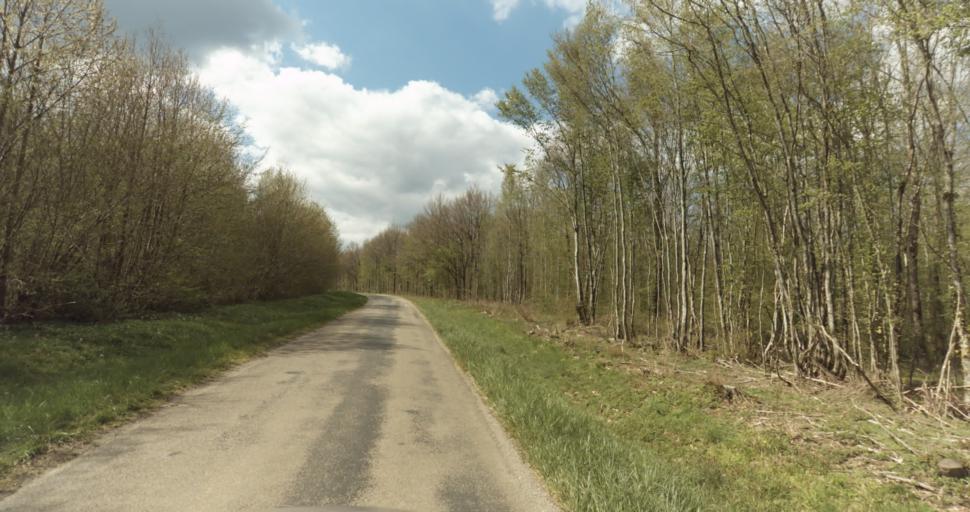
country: FR
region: Bourgogne
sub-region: Departement de la Cote-d'Or
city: Auxonne
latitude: 47.1812
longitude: 5.4565
